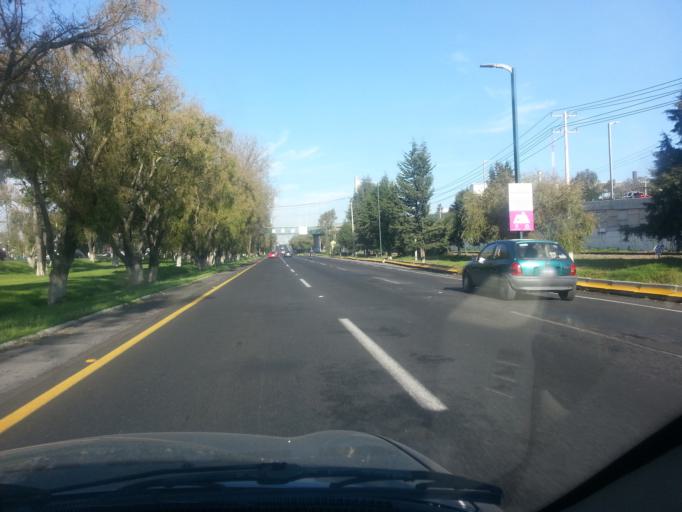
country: MX
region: Mexico
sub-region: San Mateo Atenco
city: Santa Maria la Asuncion
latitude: 19.2867
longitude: -99.5680
